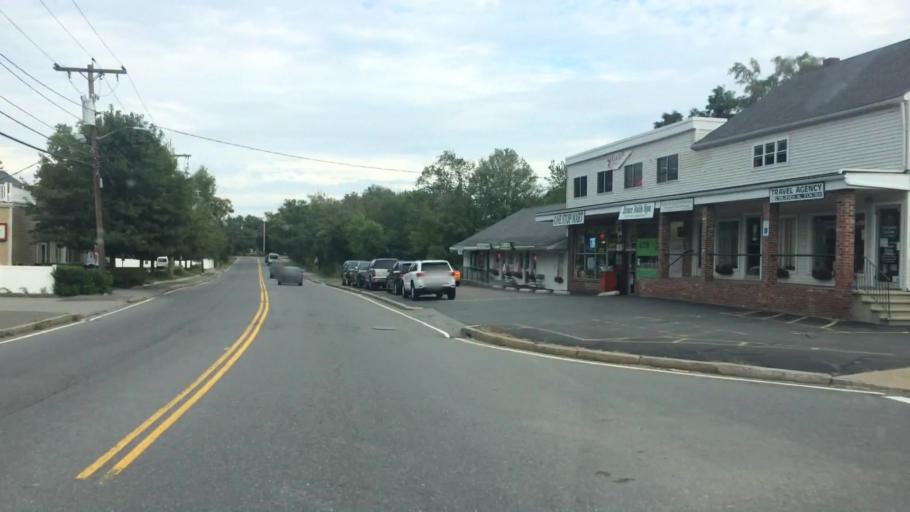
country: US
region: Massachusetts
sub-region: Middlesex County
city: Woburn
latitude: 42.4912
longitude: -71.1743
